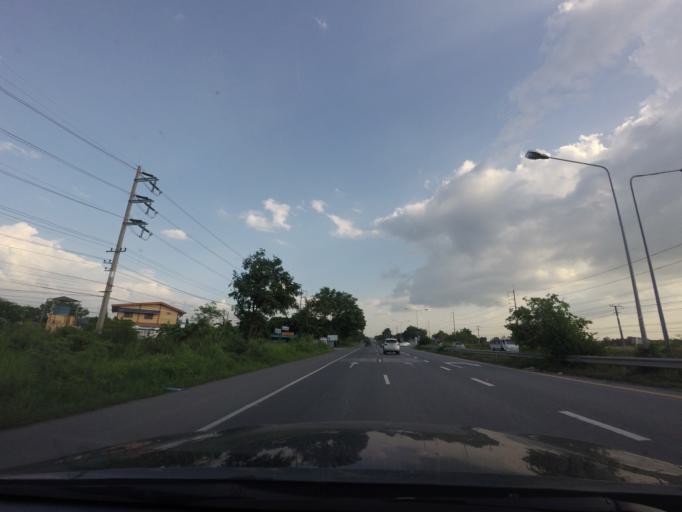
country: TH
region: Sara Buri
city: Saraburi
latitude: 14.5320
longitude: 100.8862
